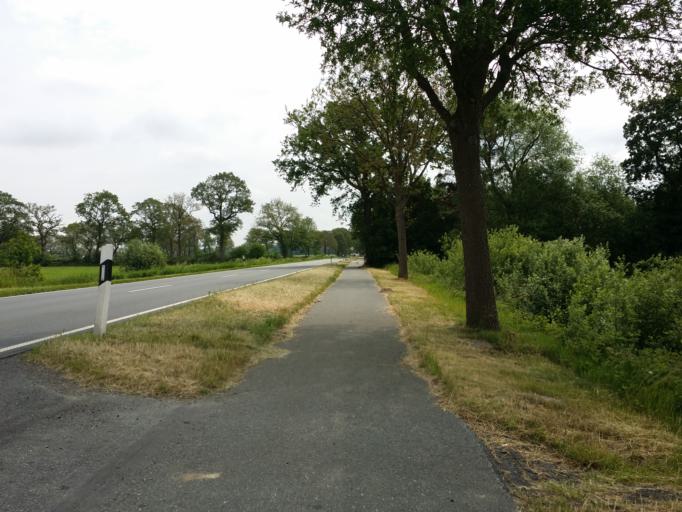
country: DE
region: Lower Saxony
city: Friedeburg
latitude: 53.4234
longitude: 7.8666
